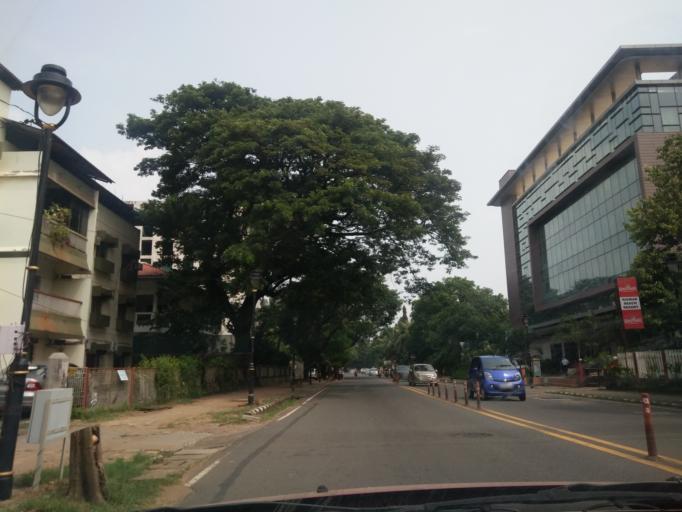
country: IN
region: Goa
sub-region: North Goa
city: Panaji
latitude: 15.4843
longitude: 73.8100
